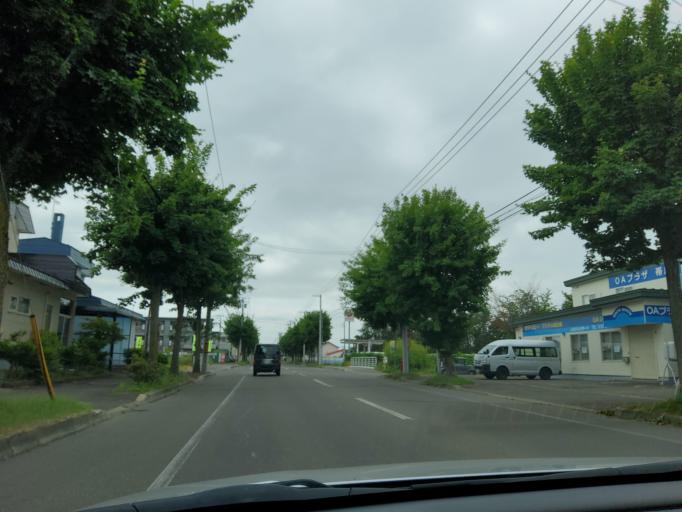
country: JP
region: Hokkaido
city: Obihiro
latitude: 42.9131
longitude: 143.1502
